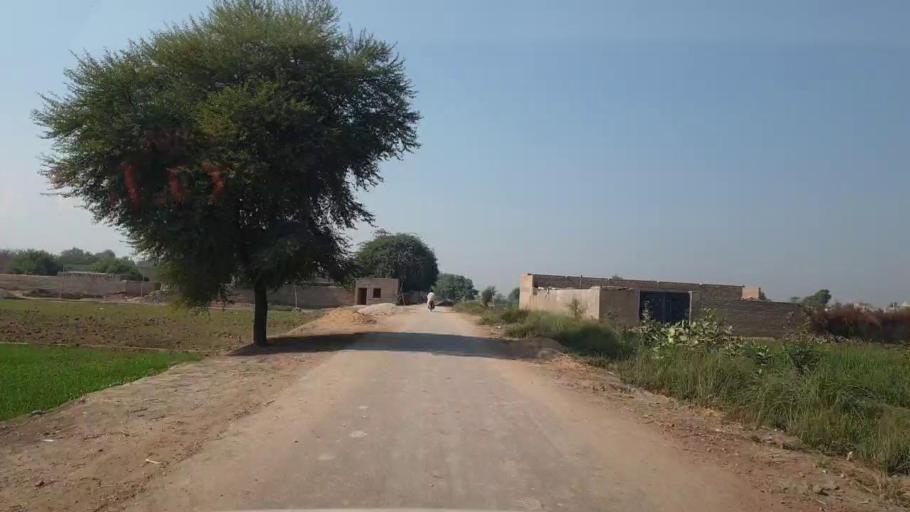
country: PK
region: Sindh
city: Bhan
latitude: 26.6413
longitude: 67.7169
